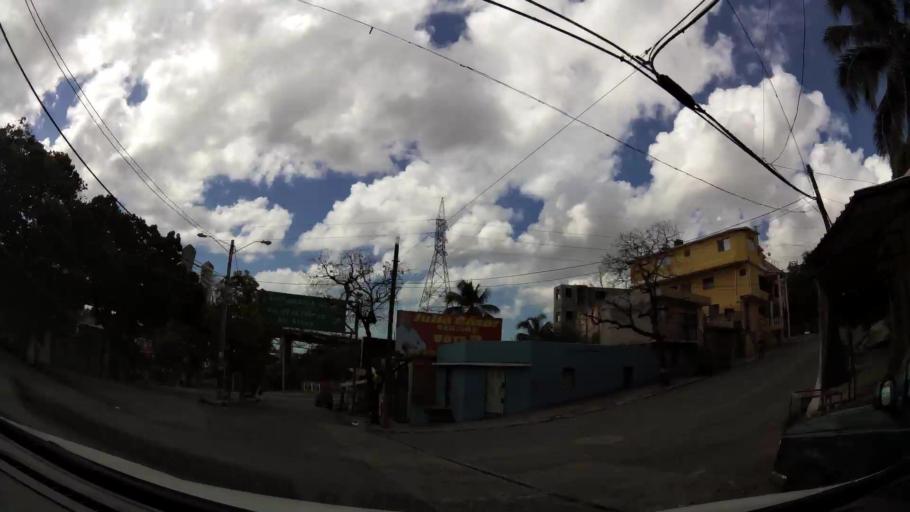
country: DO
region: Nacional
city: San Carlos
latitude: 18.4886
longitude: -69.8840
